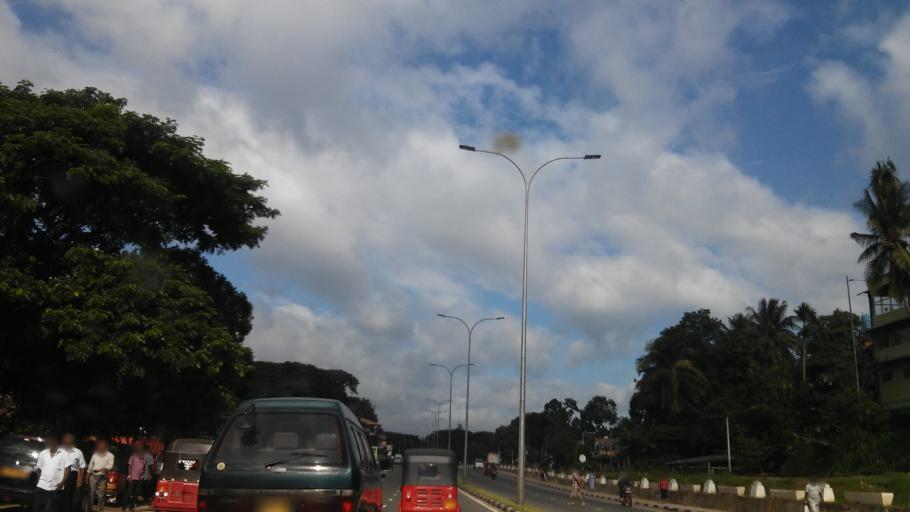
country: LK
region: Central
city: Kandy
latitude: 7.2729
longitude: 80.6099
